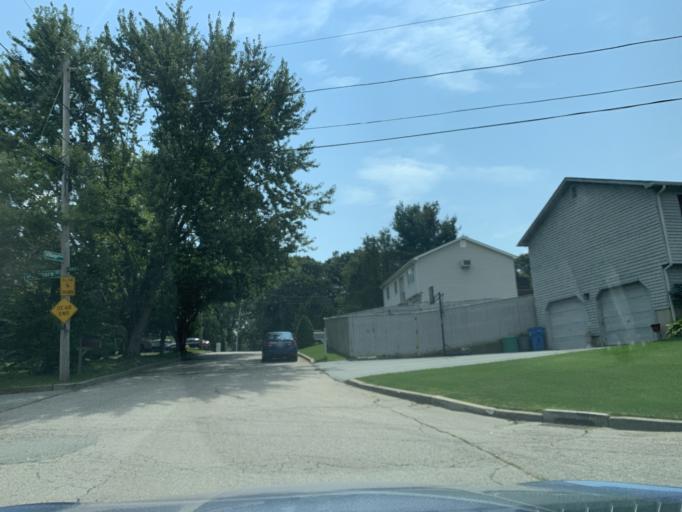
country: US
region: Rhode Island
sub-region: Providence County
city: Johnston
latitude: 41.7855
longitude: -71.4819
